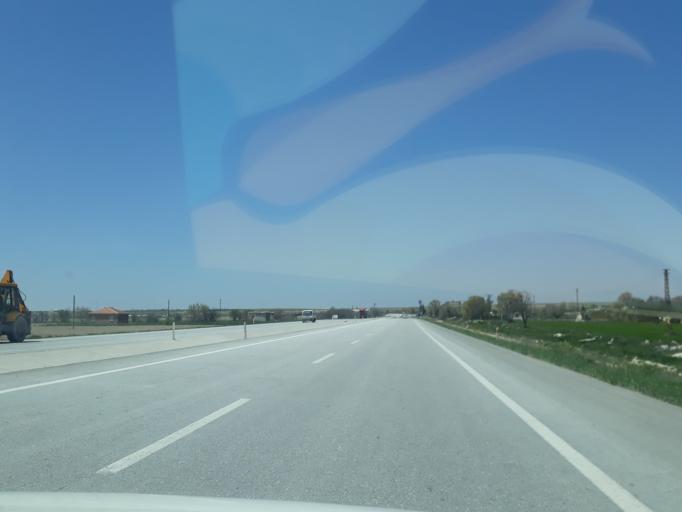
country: TR
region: Konya
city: Karapinar
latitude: 37.7159
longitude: 33.4978
